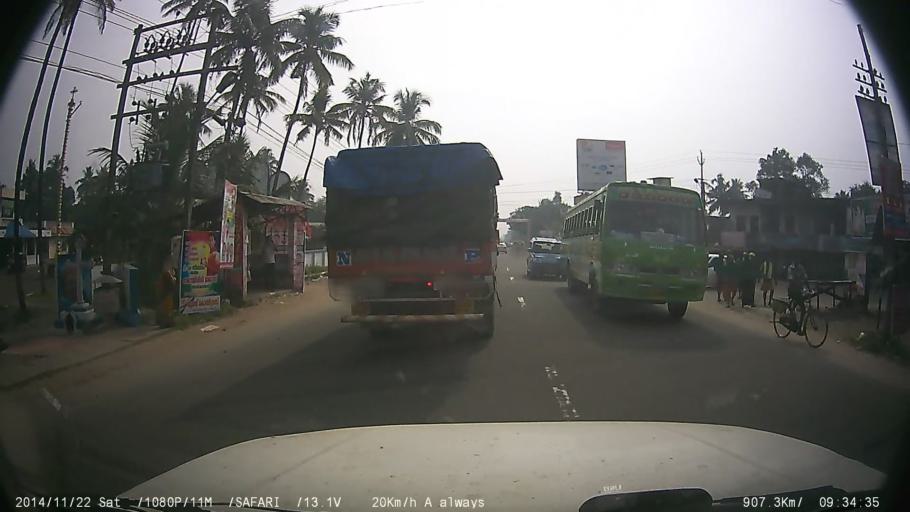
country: IN
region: Kerala
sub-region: Ernakulam
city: Angamali
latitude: 10.1709
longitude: 76.4290
